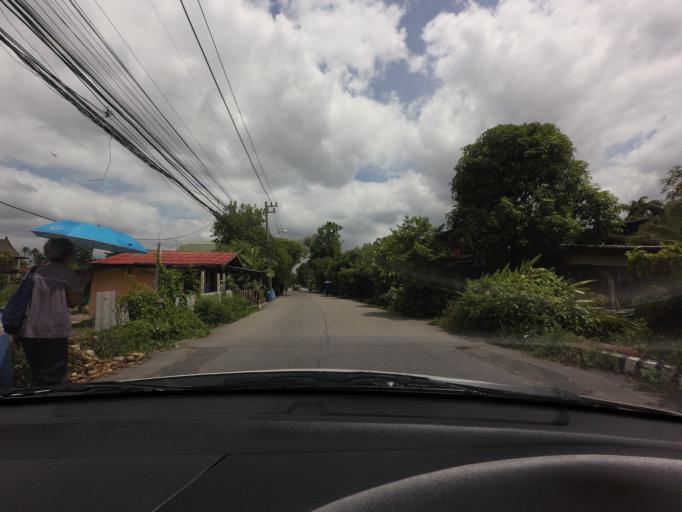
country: TH
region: Bangkok
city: Yan Nawa
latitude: 13.6825
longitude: 100.5631
